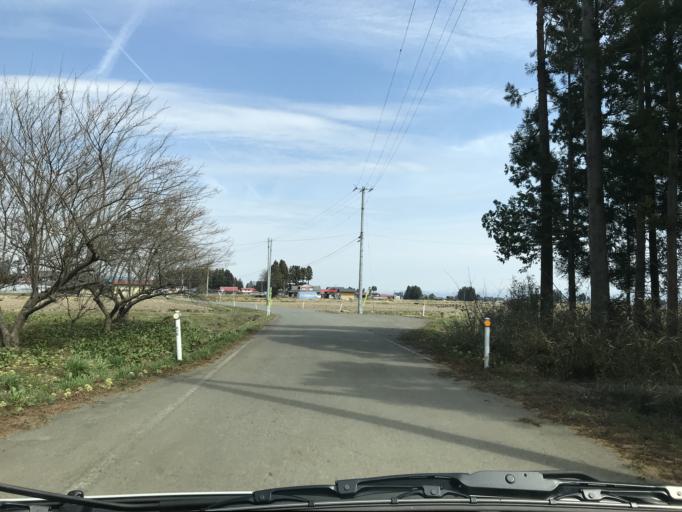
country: JP
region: Iwate
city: Mizusawa
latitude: 39.1176
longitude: 141.0859
